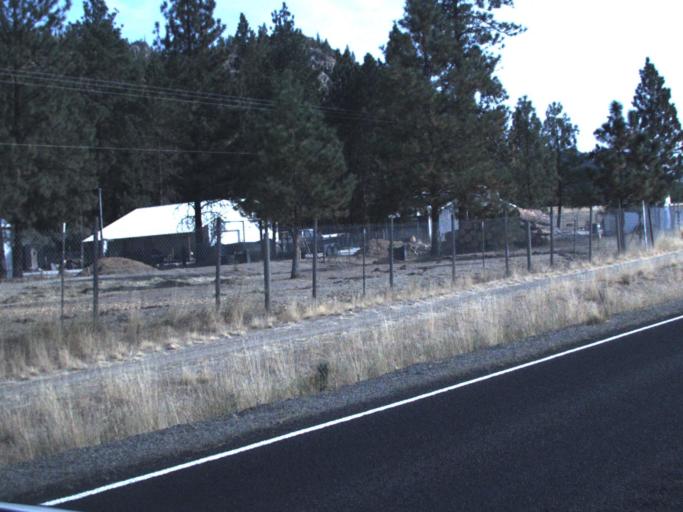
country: US
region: Washington
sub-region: Spokane County
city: Fairchild Air Force Base
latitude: 47.8414
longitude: -117.7417
